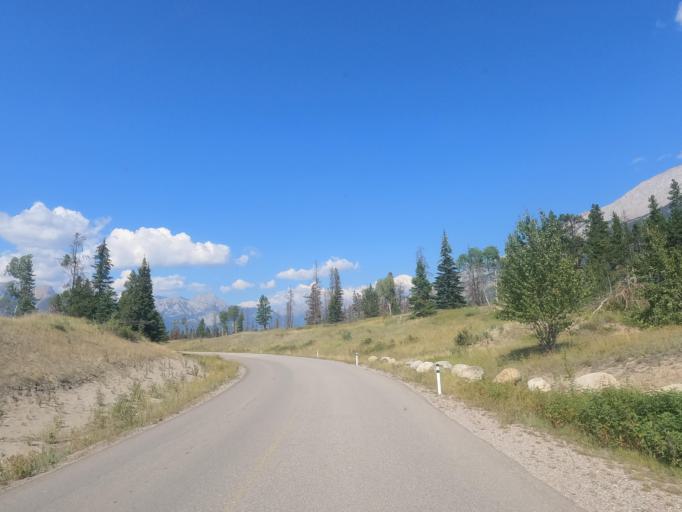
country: CA
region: Alberta
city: Jasper Park Lodge
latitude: 52.9723
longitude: -118.0607
